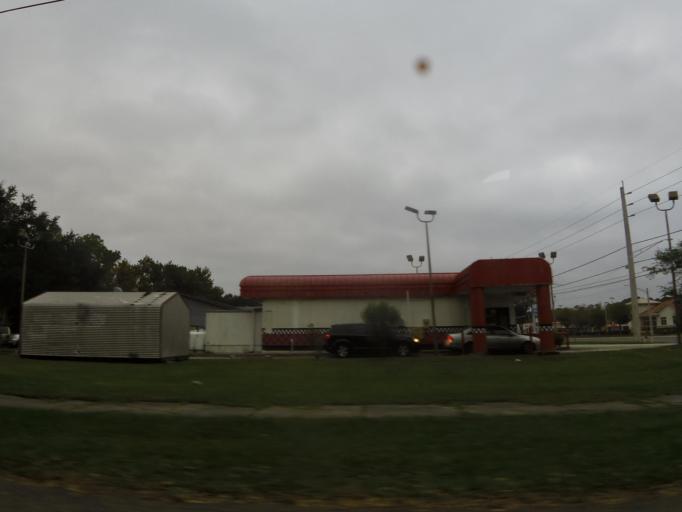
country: US
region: Florida
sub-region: Clay County
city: Bellair-Meadowbrook Terrace
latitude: 30.2480
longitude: -81.7527
